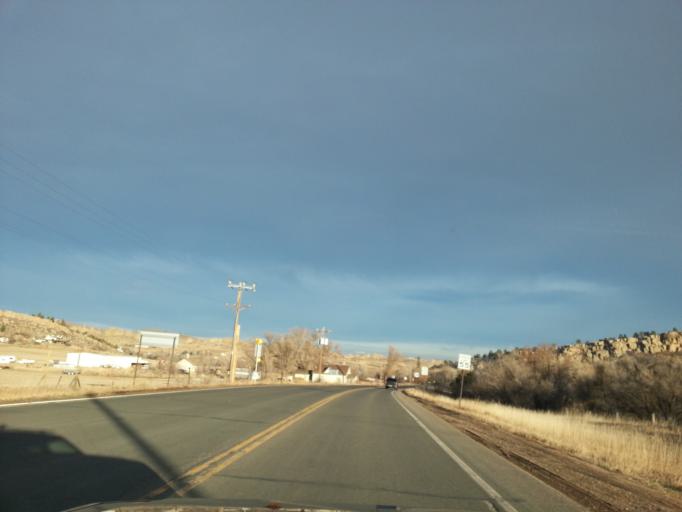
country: US
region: Colorado
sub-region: Larimer County
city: Loveland
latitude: 40.4181
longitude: -105.1876
